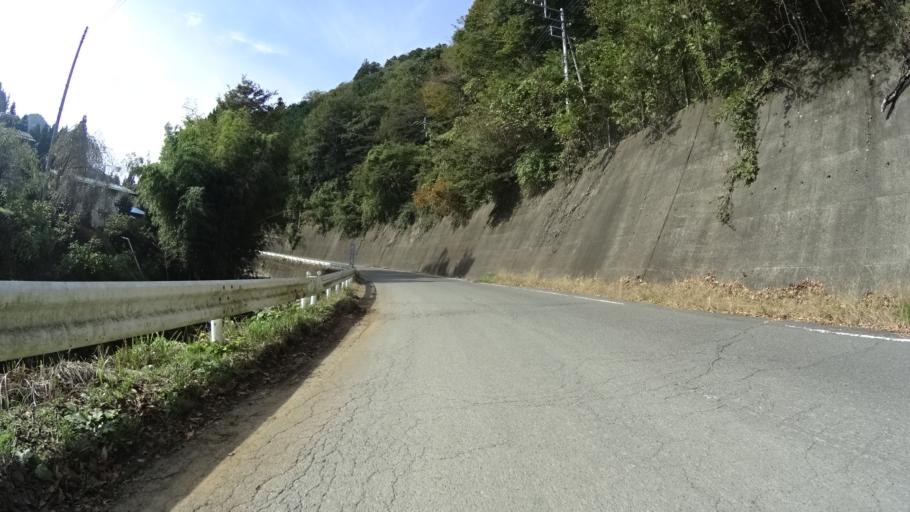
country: JP
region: Yamanashi
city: Otsuki
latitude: 35.5985
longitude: 138.9738
